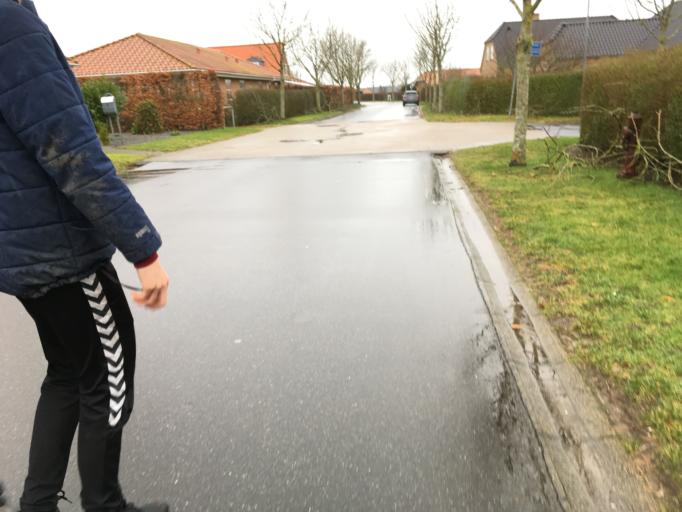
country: DK
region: Central Jutland
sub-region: Ringkobing-Skjern Kommune
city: Ringkobing
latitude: 56.0990
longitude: 8.2639
